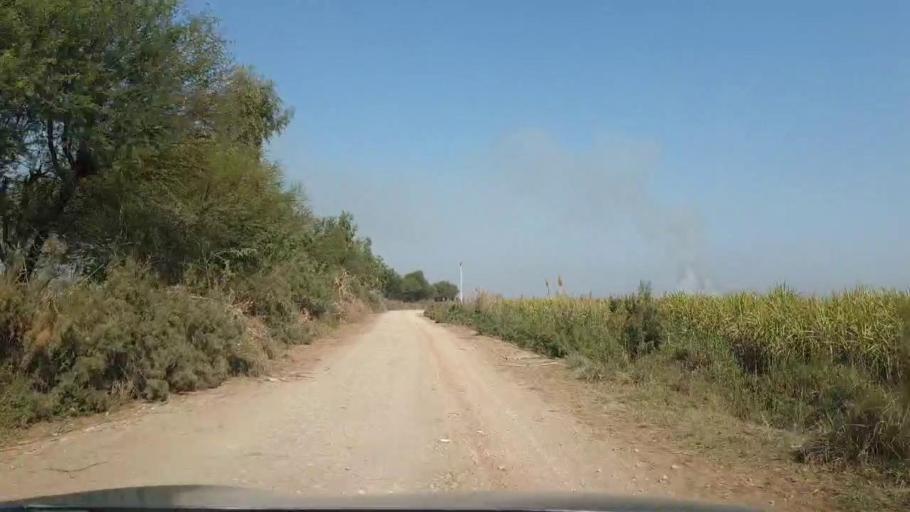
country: PK
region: Sindh
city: Berani
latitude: 25.6440
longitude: 68.8961
